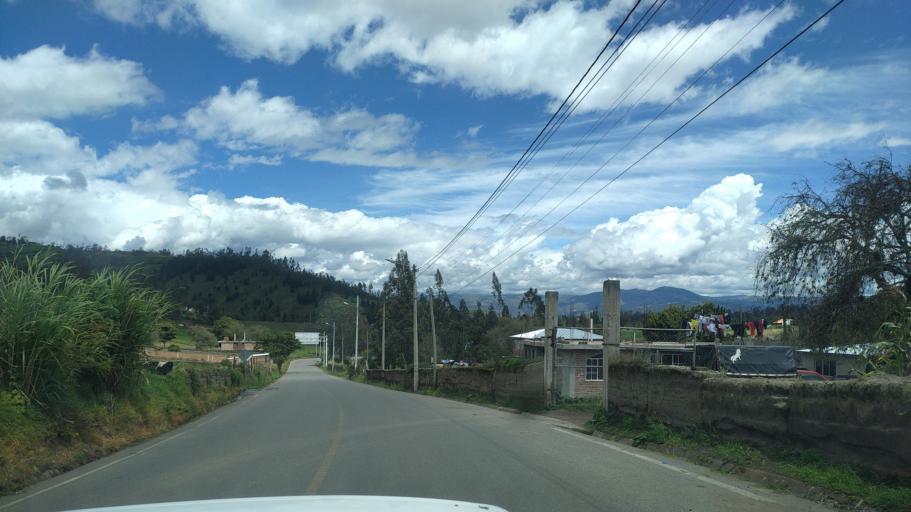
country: EC
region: Chimborazo
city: Riobamba
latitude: -1.6601
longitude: -78.5779
